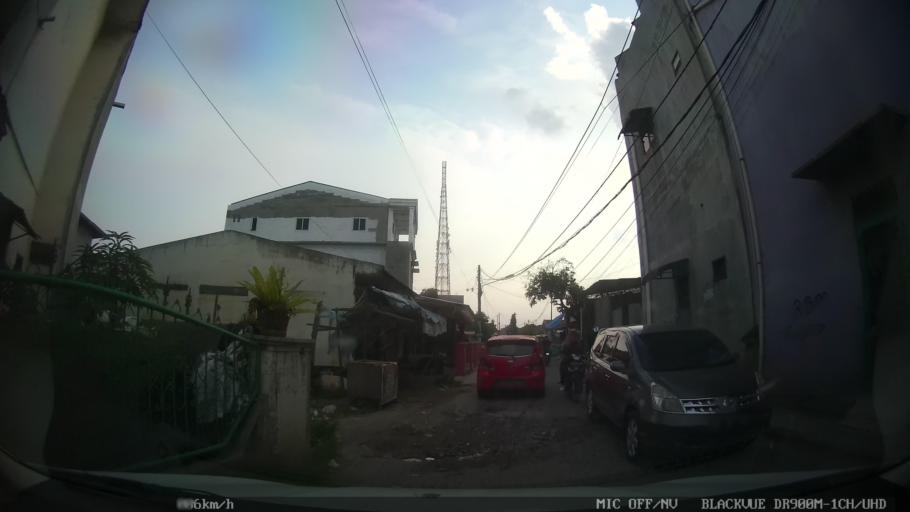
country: ID
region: North Sumatra
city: Medan
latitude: 3.5961
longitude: 98.7451
